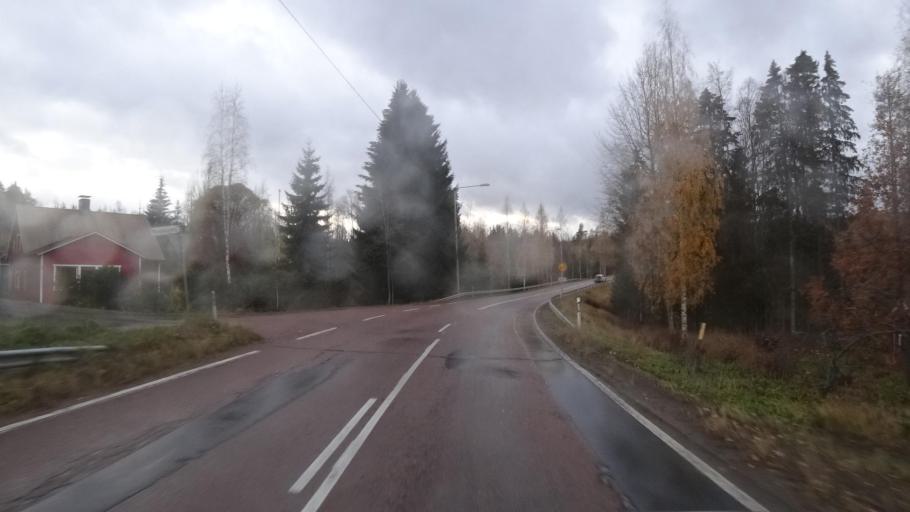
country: FI
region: Southern Savonia
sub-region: Mikkeli
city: Kangasniemi
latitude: 62.0987
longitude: 26.7434
